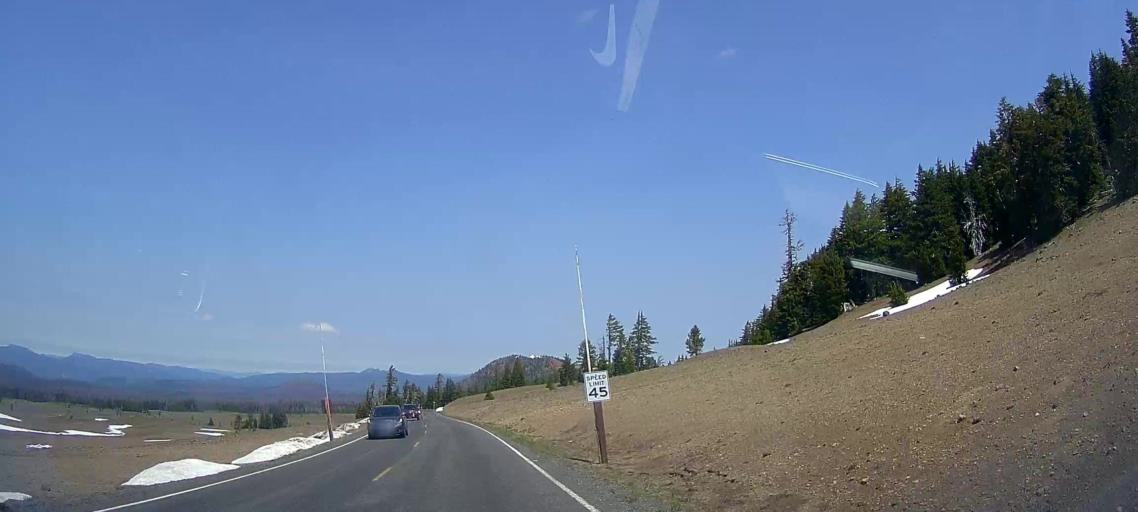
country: US
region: Oregon
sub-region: Jackson County
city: Shady Cove
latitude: 42.9690
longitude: -122.1515
